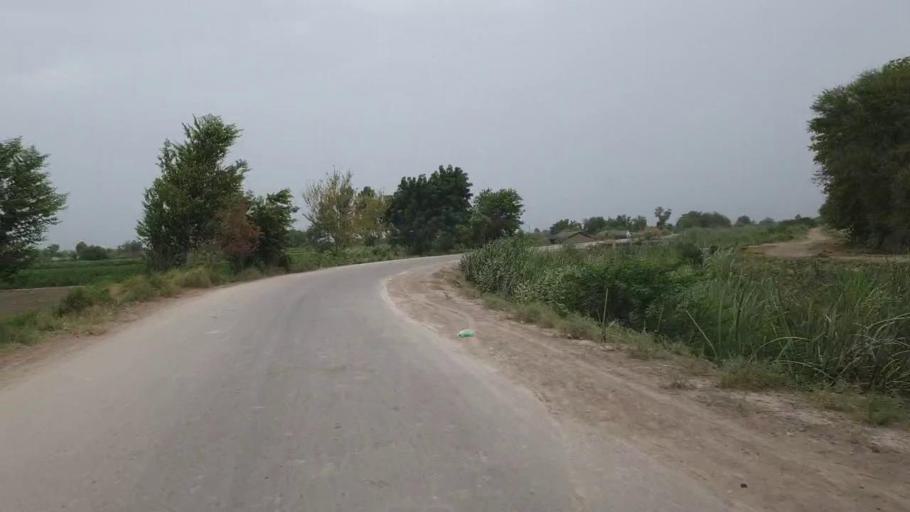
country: PK
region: Sindh
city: Bandhi
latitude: 26.5462
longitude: 68.2192
